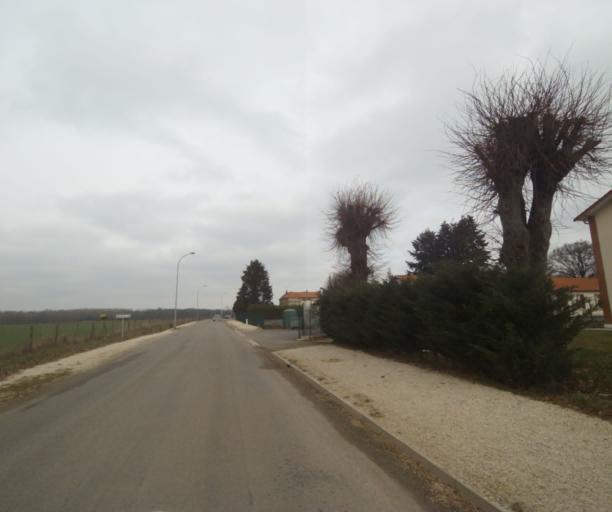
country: FR
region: Champagne-Ardenne
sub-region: Departement de la Haute-Marne
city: Villiers-en-Lieu
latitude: 48.6800
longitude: 4.8718
